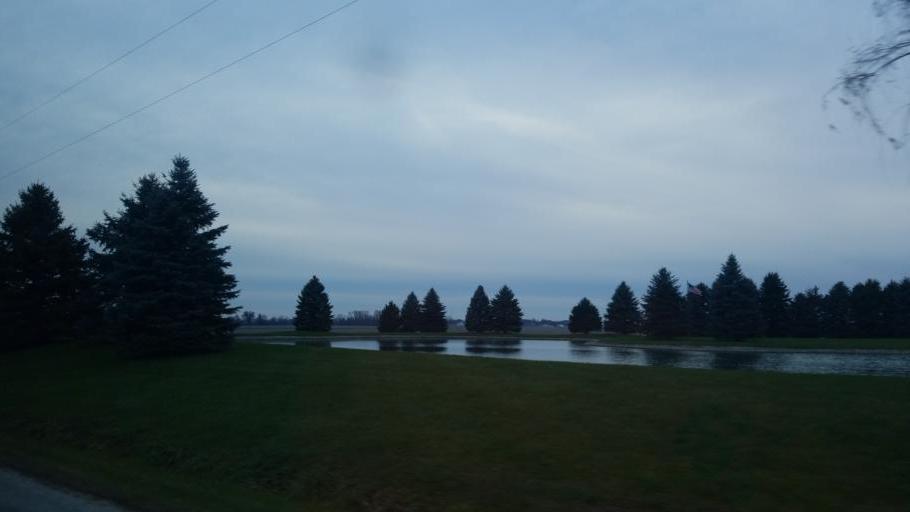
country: US
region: Indiana
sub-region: Adams County
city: Decatur
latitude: 40.7797
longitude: -84.8800
